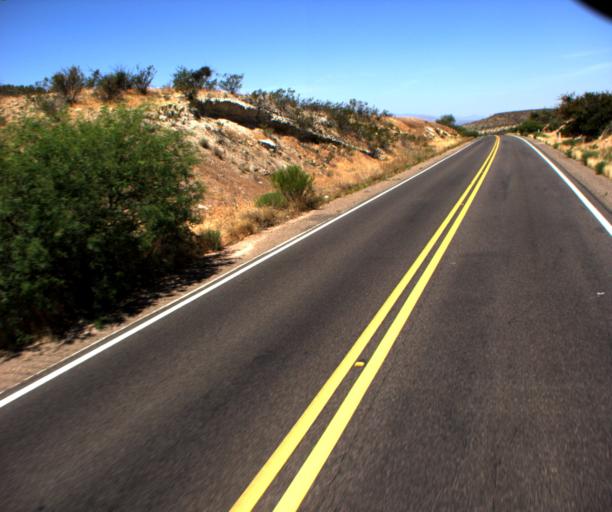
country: US
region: Arizona
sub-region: Gila County
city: Peridot
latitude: 33.2851
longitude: -110.3487
